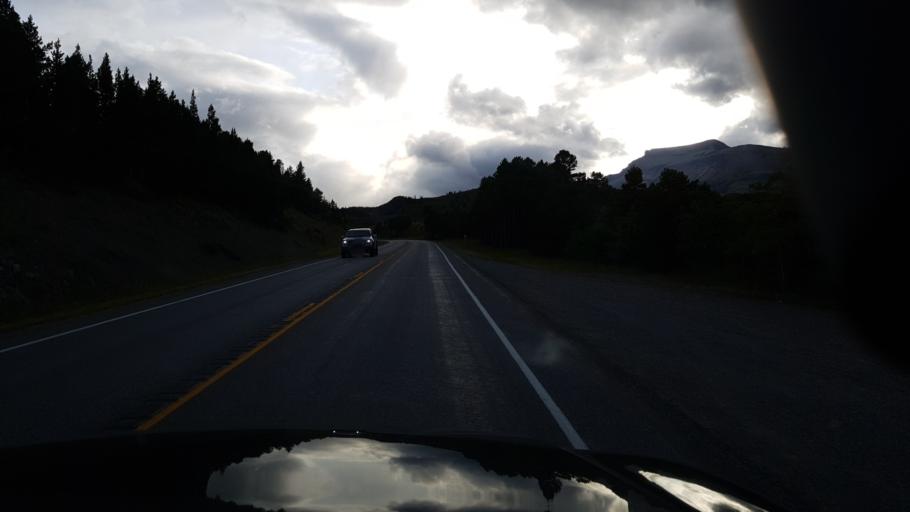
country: US
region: Montana
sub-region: Glacier County
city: South Browning
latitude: 48.4046
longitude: -113.2455
